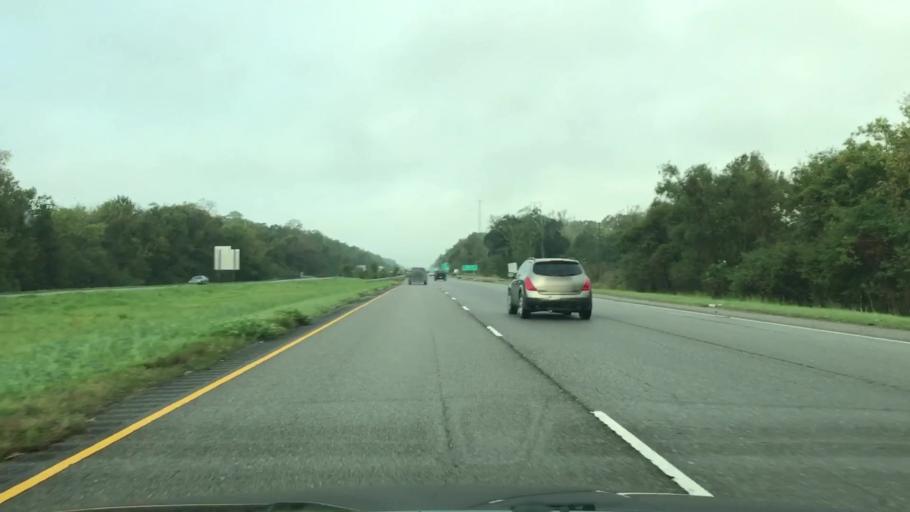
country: US
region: Louisiana
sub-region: Terrebonne Parish
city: Gray
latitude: 29.6821
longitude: -90.7578
